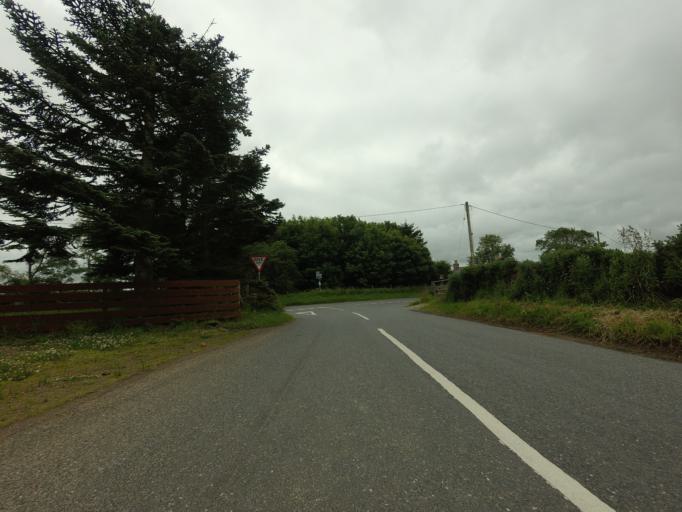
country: GB
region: Scotland
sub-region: Aberdeenshire
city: Rosehearty
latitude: 57.5397
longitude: -2.1886
